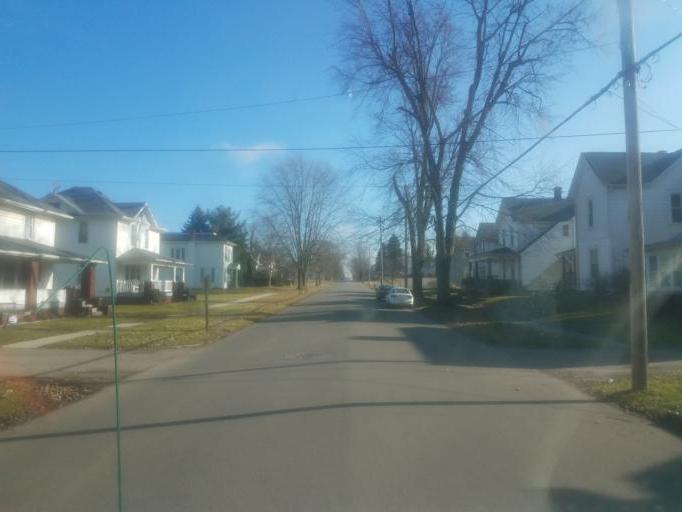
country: US
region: Ohio
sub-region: Crawford County
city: Galion
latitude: 40.7352
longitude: -82.7940
